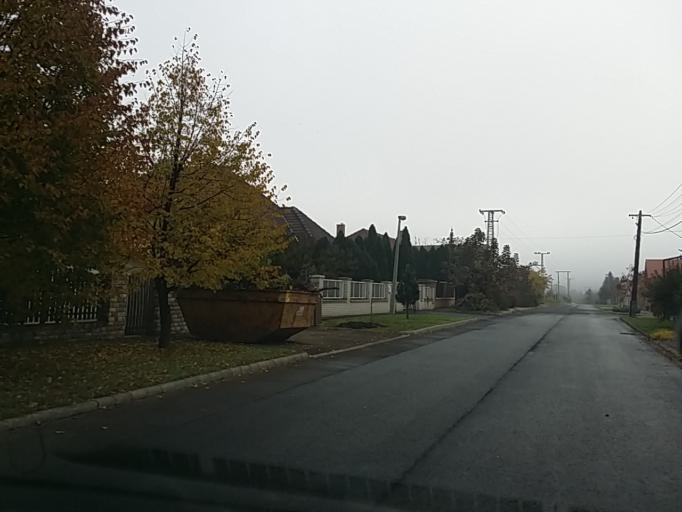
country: HU
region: Heves
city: Gyongyossolymos
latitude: 47.8000
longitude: 19.9348
